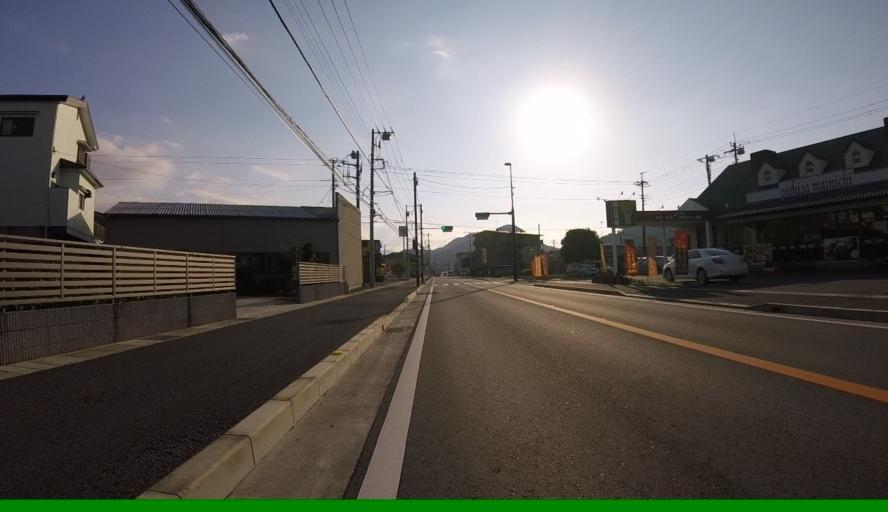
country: JP
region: Shizuoka
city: Mishima
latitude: 35.0952
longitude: 138.9043
